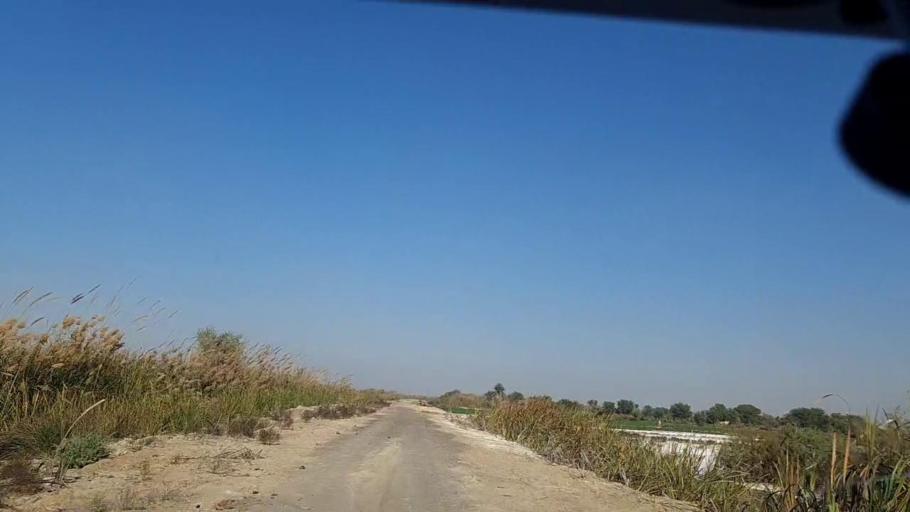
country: PK
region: Sindh
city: Khanpur
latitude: 27.5942
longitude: 69.3772
